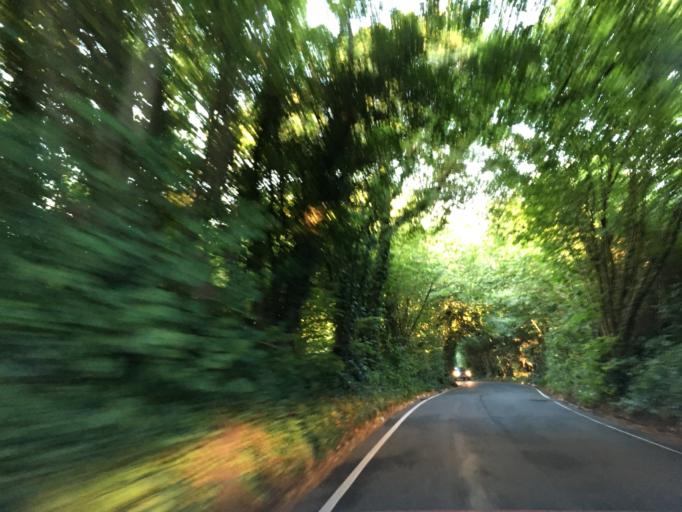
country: GB
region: England
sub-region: Bath and North East Somerset
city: Whitchurch
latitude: 51.4186
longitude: -2.5336
